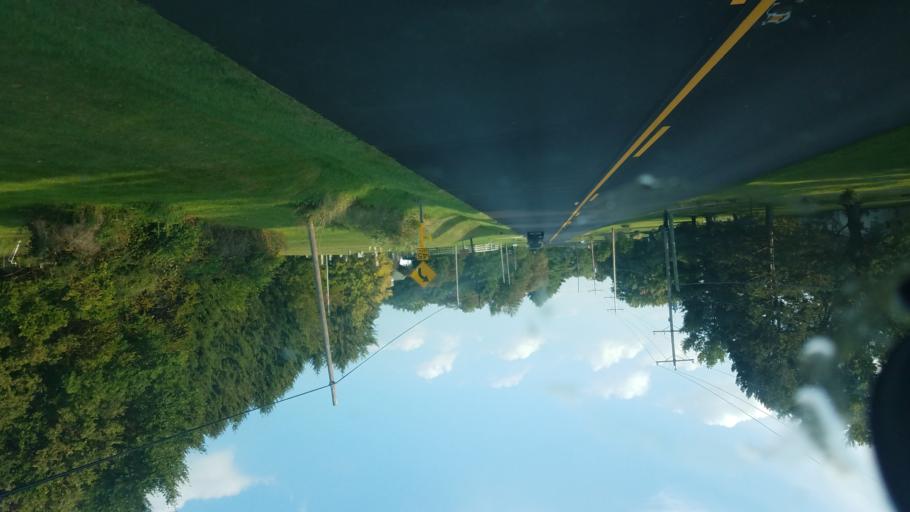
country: US
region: Ohio
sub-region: Franklin County
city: New Albany
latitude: 40.1058
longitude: -82.7771
